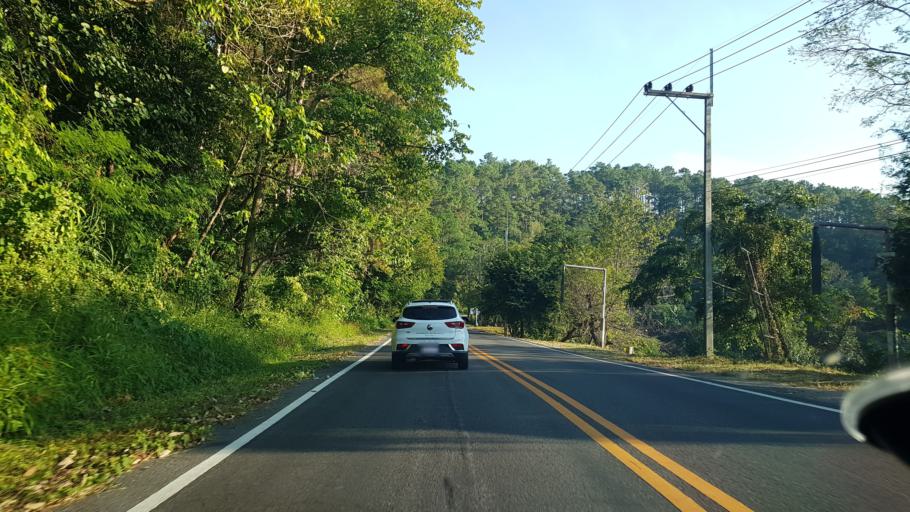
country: TH
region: Chiang Rai
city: Mae Fa Luang
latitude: 20.3061
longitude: 99.8166
